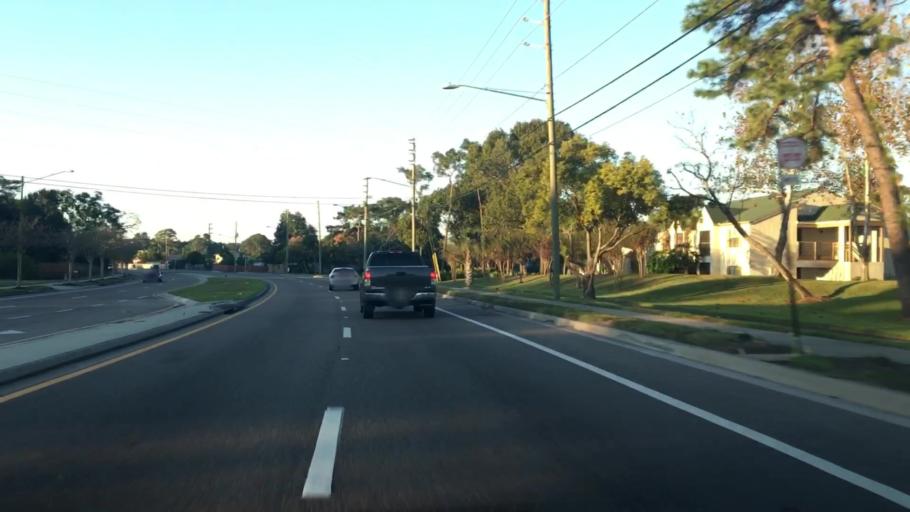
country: US
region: Florida
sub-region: Orange County
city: Azalea Park
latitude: 28.5200
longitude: -81.2882
